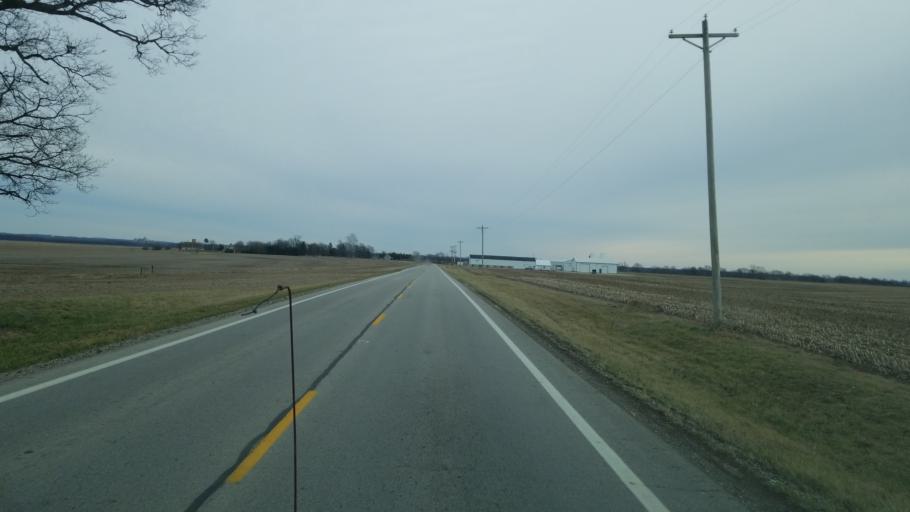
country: US
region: Ohio
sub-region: Pickaway County
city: Circleville
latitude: 39.6109
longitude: -83.0045
